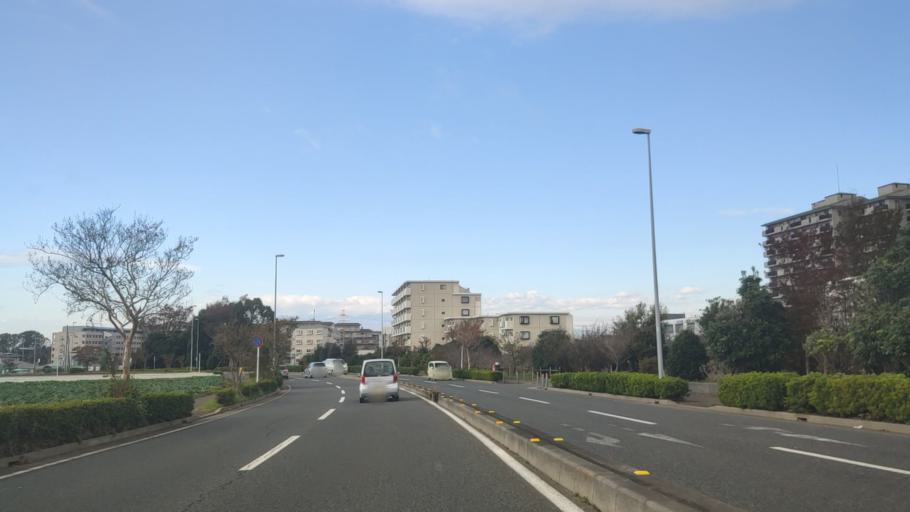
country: JP
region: Kanagawa
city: Minami-rinkan
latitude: 35.4285
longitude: 139.4979
